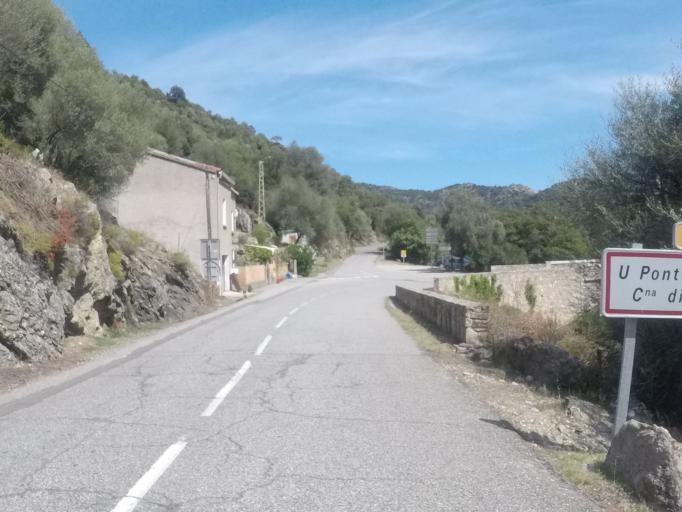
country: FR
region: Corsica
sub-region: Departement de la Haute-Corse
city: Corte
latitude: 42.3835
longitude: 9.1373
